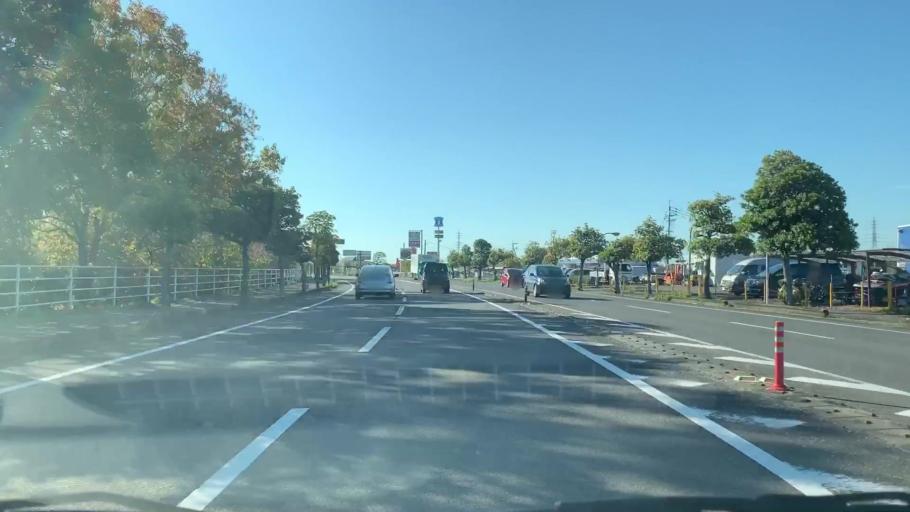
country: JP
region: Saga Prefecture
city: Saga-shi
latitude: 33.3141
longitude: 130.2758
